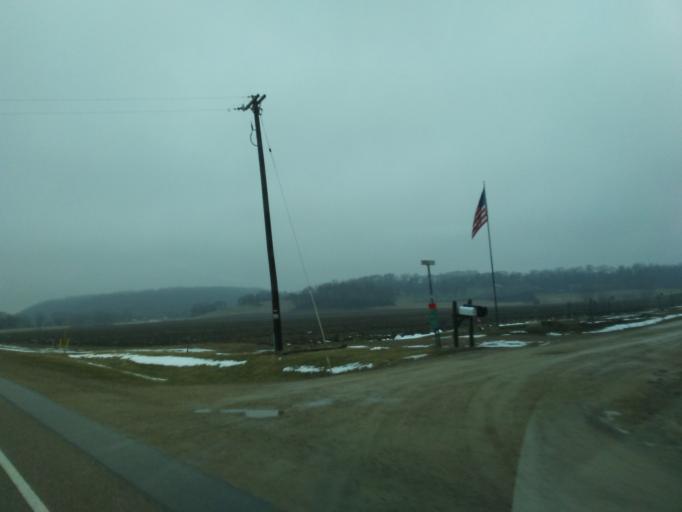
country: US
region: Wisconsin
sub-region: Dane County
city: Black Earth
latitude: 43.1355
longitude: -89.7345
